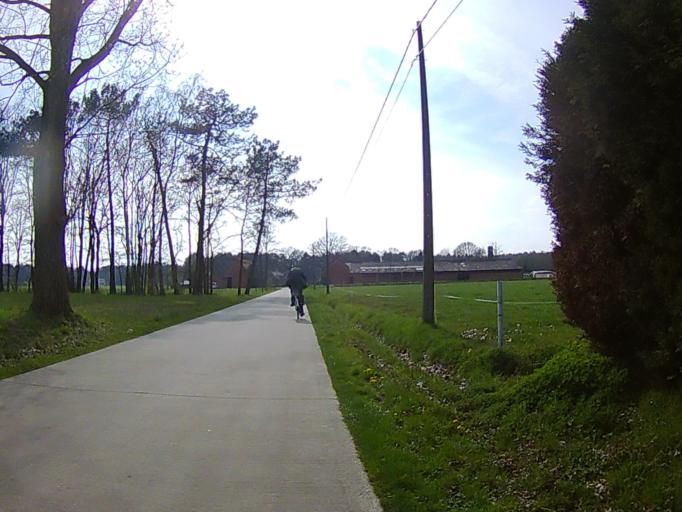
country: BE
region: Flanders
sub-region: Provincie Antwerpen
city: Kasterlee
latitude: 51.2126
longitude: 4.9189
